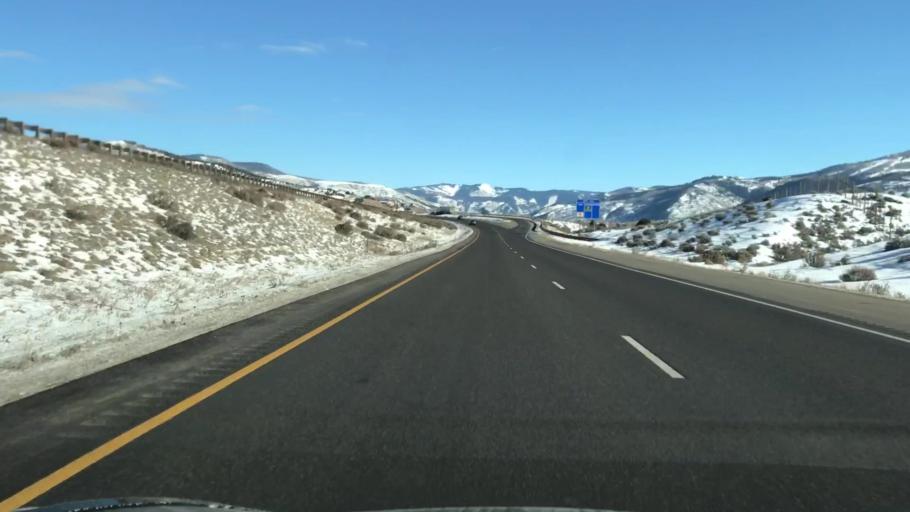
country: US
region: Colorado
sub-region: Eagle County
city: Edwards
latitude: 39.6544
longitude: -106.6147
